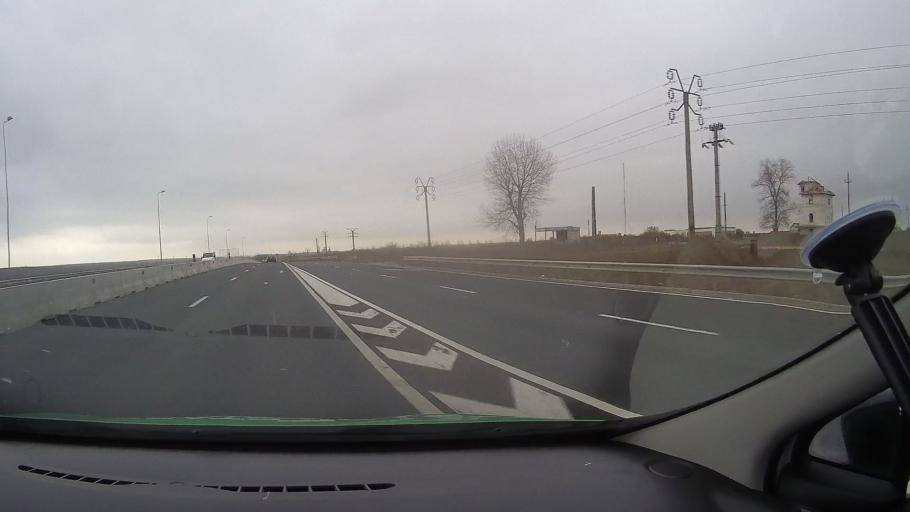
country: RO
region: Constanta
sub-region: Comuna Cumpana
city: Cumpana
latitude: 44.1666
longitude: 28.5441
